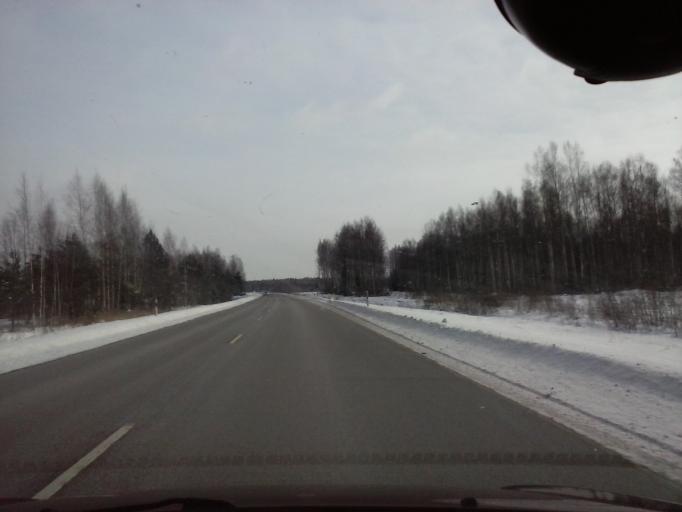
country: EE
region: Paernumaa
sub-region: Saarde vald
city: Kilingi-Nomme
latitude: 58.1747
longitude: 24.8065
